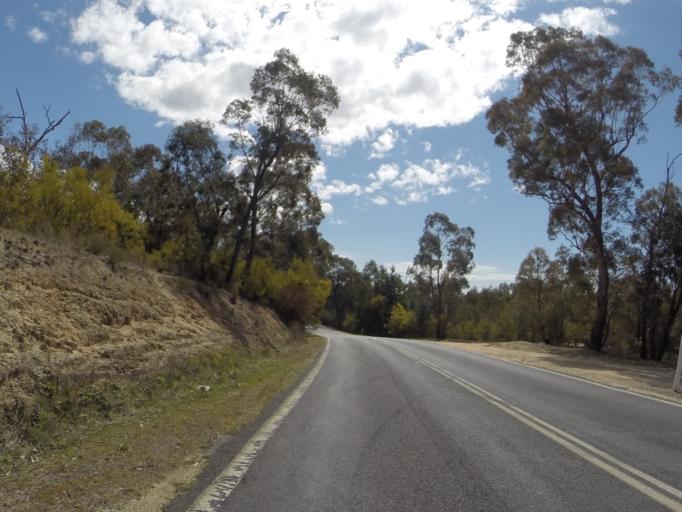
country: AU
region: Australian Capital Territory
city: Macquarie
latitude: -35.3550
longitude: 148.9445
